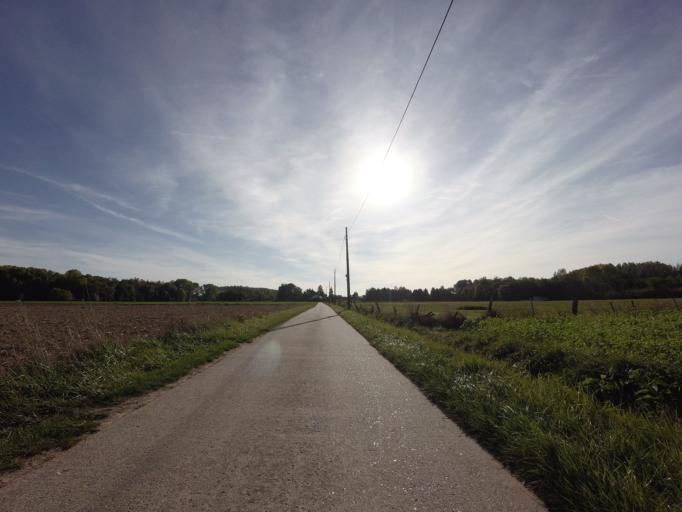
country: BE
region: Flanders
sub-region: Provincie Vlaams-Brabant
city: Kampenhout
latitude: 50.9130
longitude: 4.5970
